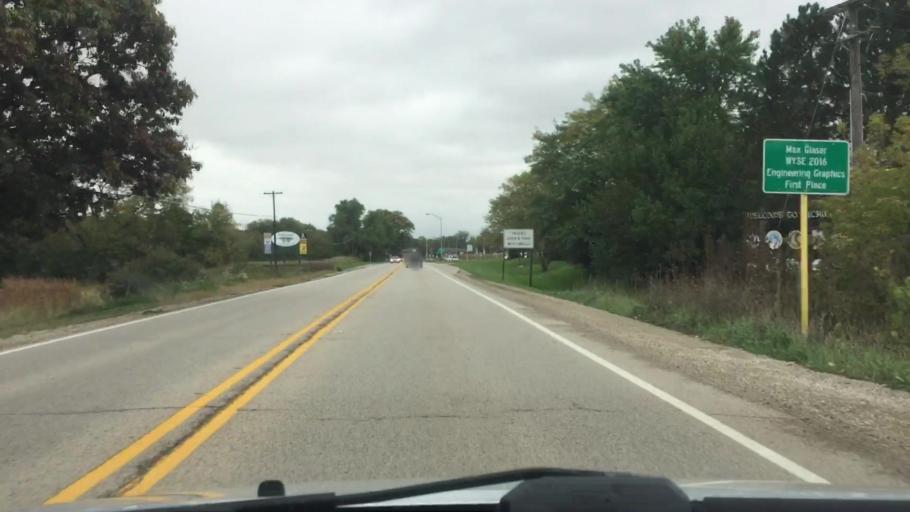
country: US
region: Wisconsin
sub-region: Walworth County
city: Genoa City
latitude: 42.4937
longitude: -88.3106
